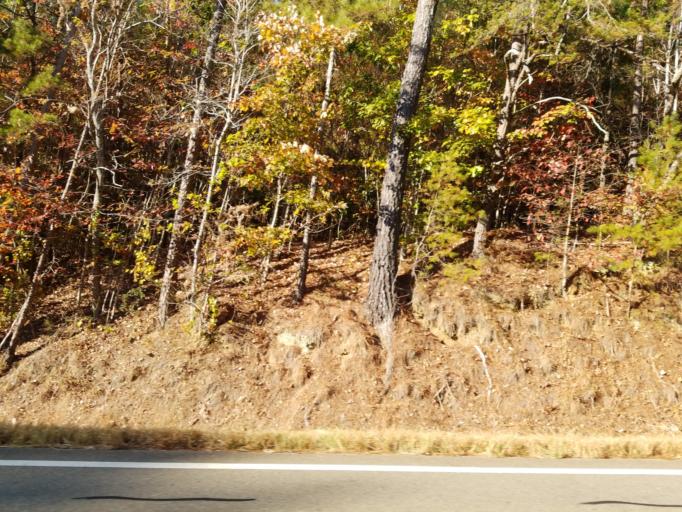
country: US
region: Georgia
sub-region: Pickens County
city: Jasper
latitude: 34.5220
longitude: -84.4960
